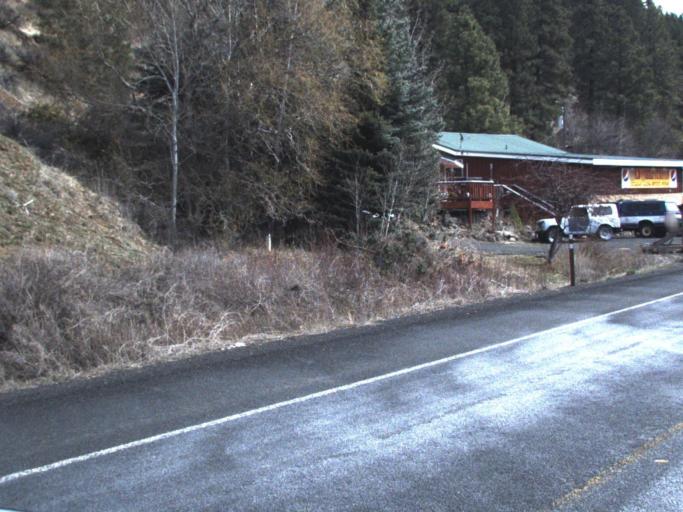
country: US
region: Washington
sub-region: Kittitas County
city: Cle Elum
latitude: 46.9152
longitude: -121.0392
